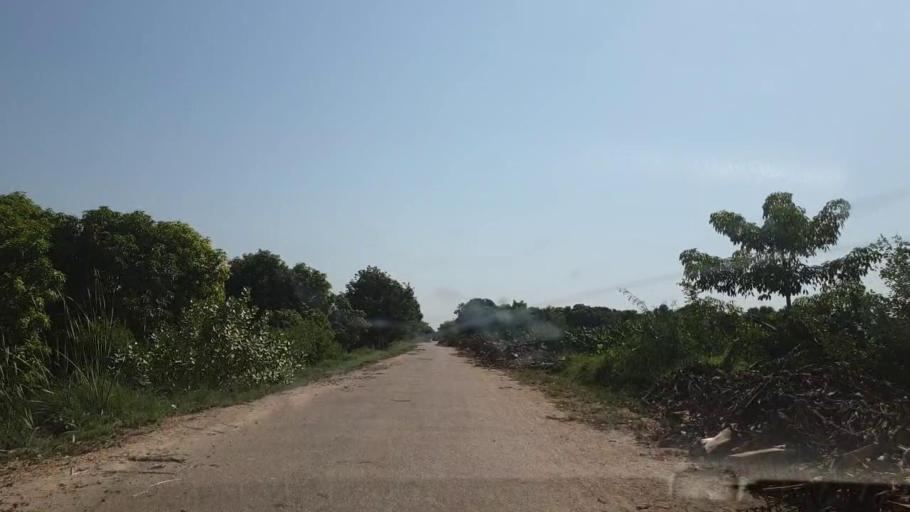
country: PK
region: Sindh
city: Tando Jam
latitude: 25.4151
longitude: 68.5821
